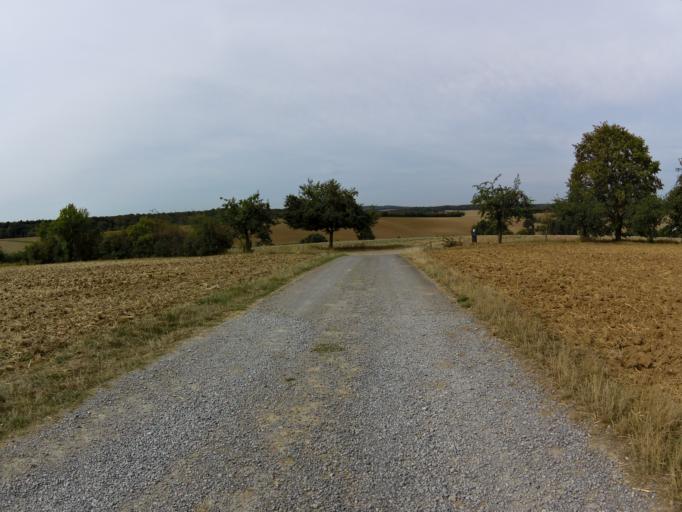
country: DE
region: Bavaria
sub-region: Regierungsbezirk Unterfranken
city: Waldbuttelbrunn
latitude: 49.7797
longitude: 9.8393
